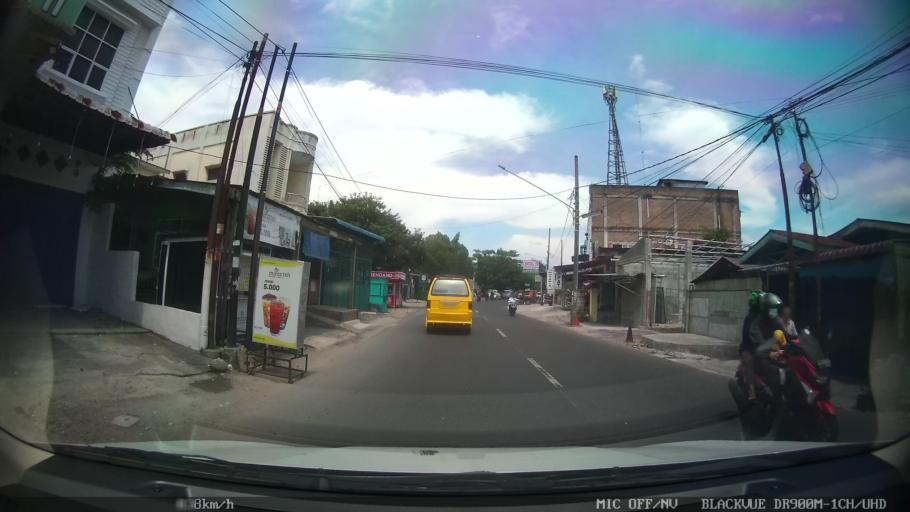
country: ID
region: North Sumatra
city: Binjai
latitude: 3.5998
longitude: 98.4874
